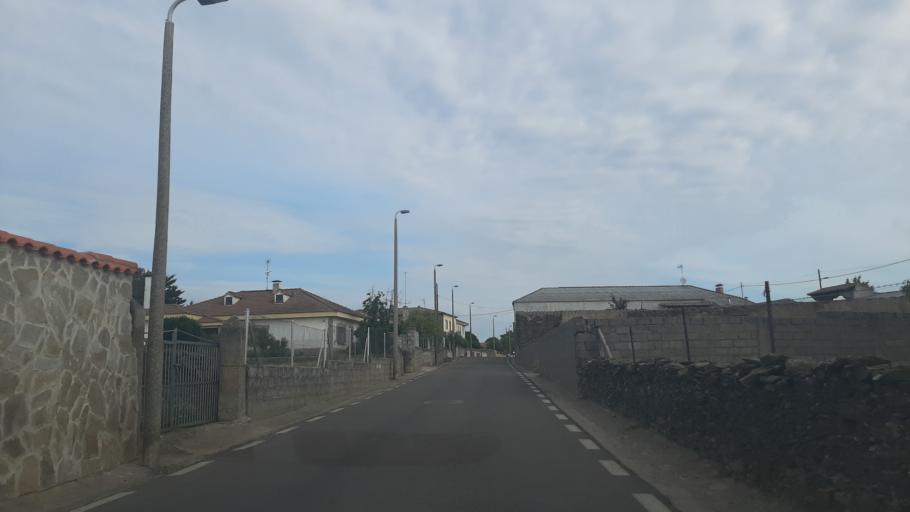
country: ES
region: Castille and Leon
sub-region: Provincia de Salamanca
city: Gallegos de Arganan
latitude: 40.6302
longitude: -6.7042
